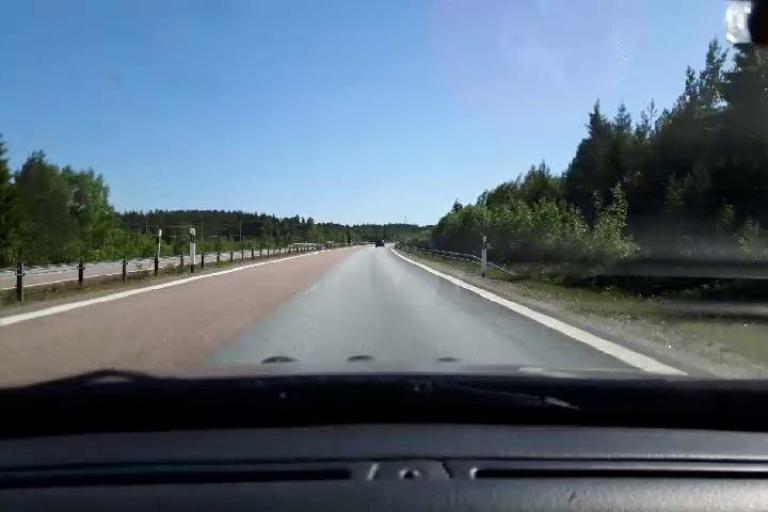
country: SE
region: Gaevleborg
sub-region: Soderhamns Kommun
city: Soderhamn
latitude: 61.4085
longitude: 16.9936
